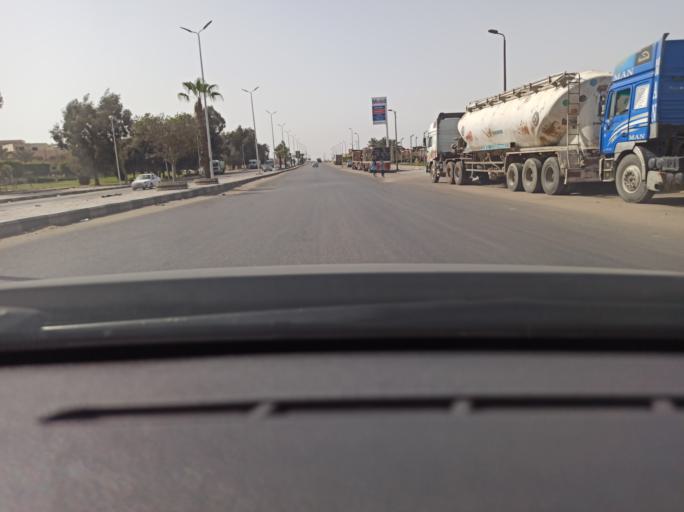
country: EG
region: Muhafazat al Qahirah
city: Halwan
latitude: 29.8237
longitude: 31.3534
